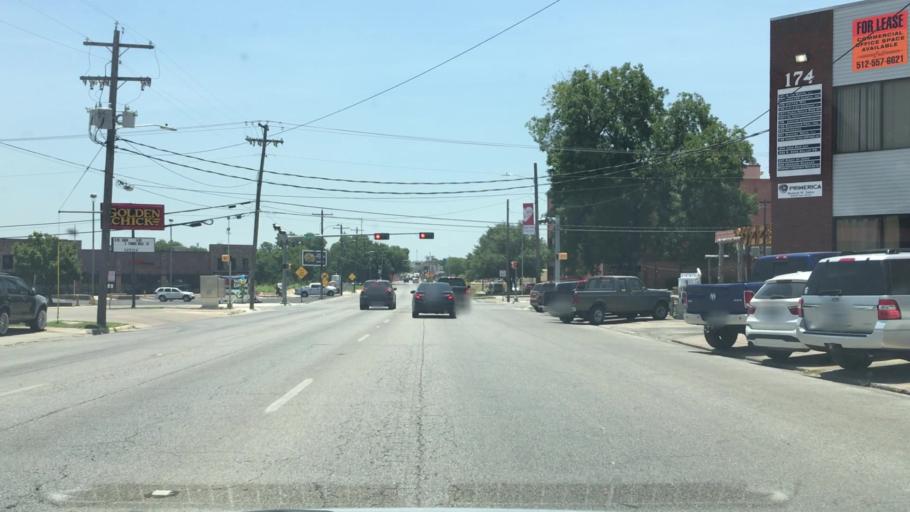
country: US
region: Texas
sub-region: Hays County
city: San Marcos
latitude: 29.8808
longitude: -97.9411
